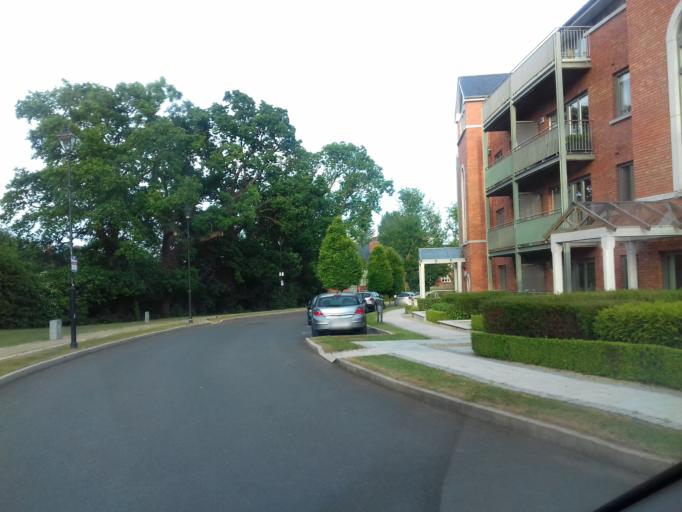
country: IE
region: Leinster
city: Castleknock
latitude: 53.3680
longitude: -6.3589
